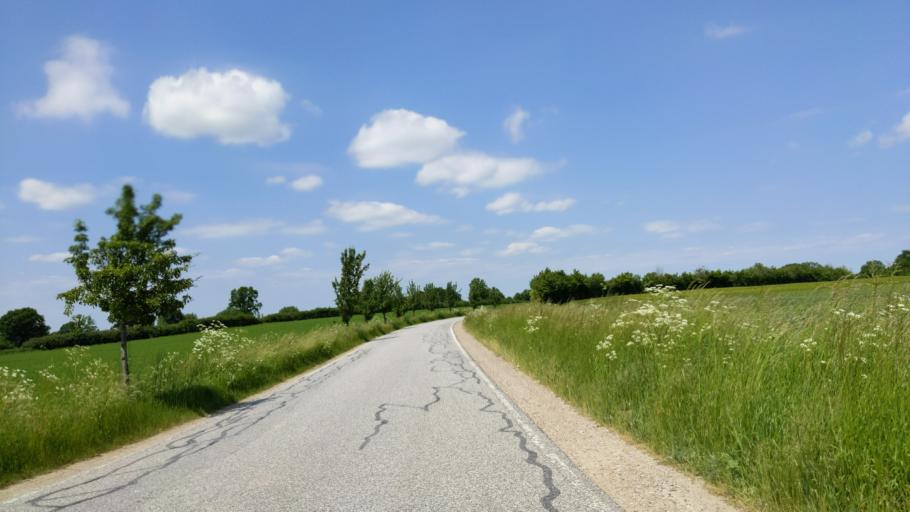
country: DE
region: Schleswig-Holstein
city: Krummesse
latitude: 53.8231
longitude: 10.6644
